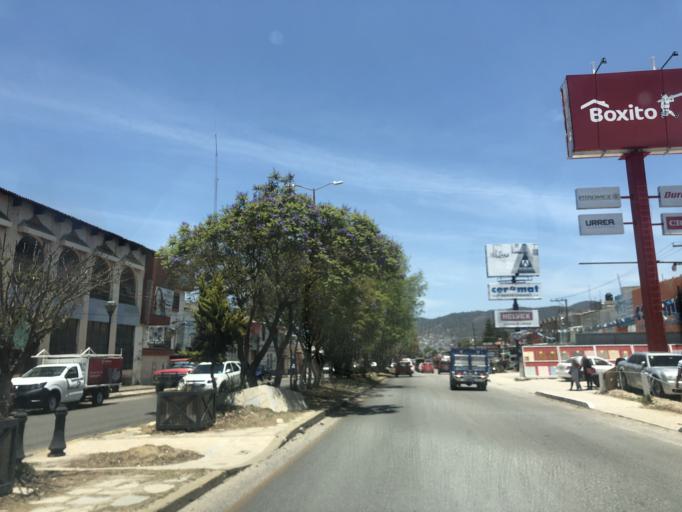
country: MX
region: Chiapas
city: San Cristobal de las Casas
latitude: 16.7251
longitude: -92.6351
